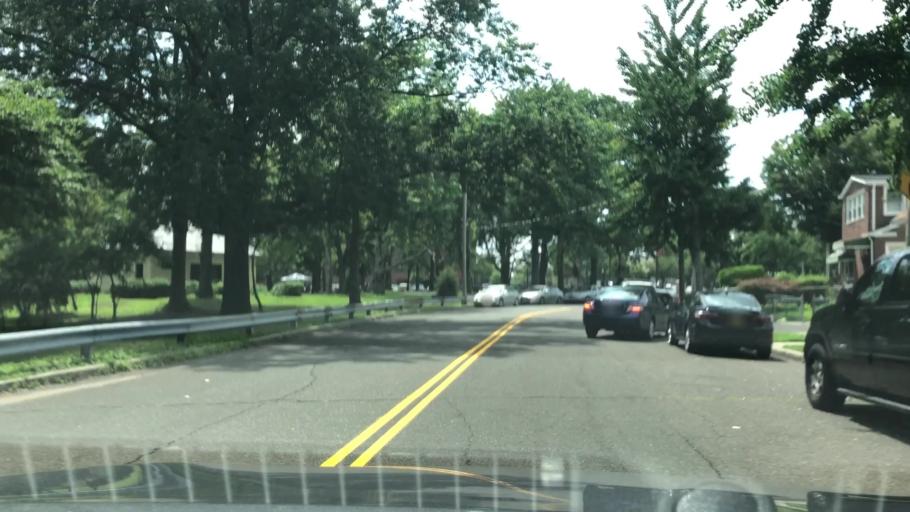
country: US
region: New York
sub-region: Queens County
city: Jamaica
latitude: 40.6751
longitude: -73.7872
